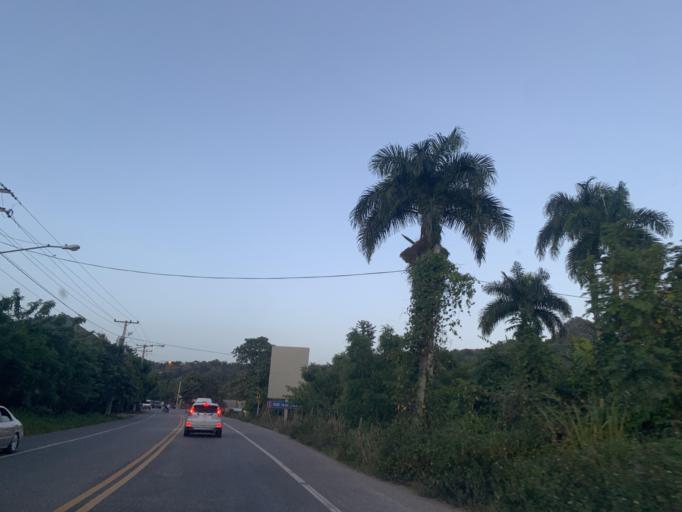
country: DO
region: Puerto Plata
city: Imbert
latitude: 19.7990
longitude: -70.7836
